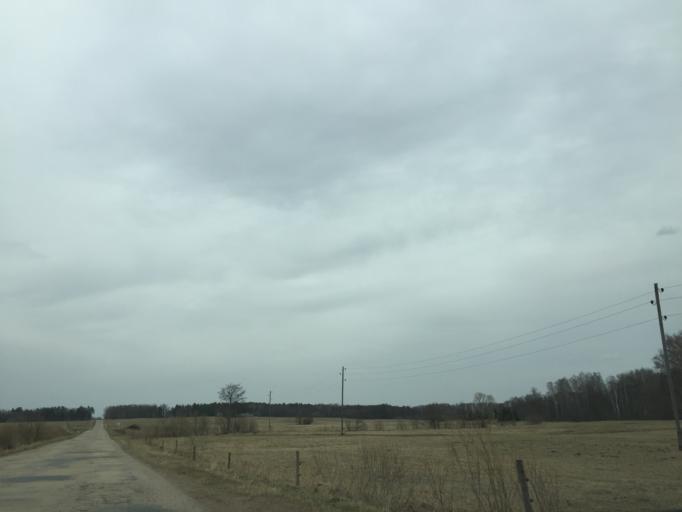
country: LV
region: Ilukste
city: Ilukste
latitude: 56.0304
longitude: 26.2754
